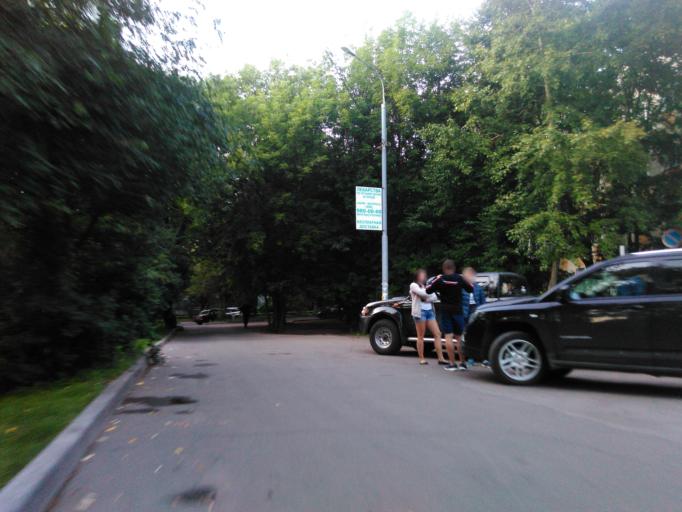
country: RU
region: Moscow
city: Yaroslavskiy
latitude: 55.8722
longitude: 37.7094
